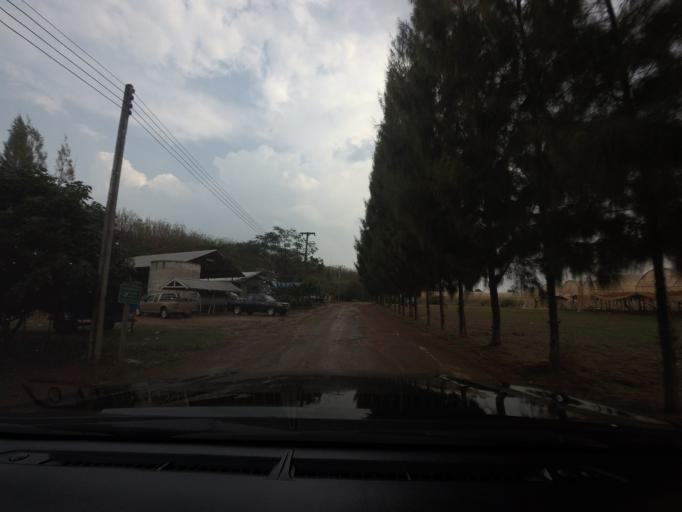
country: TH
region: Nakhon Ratchasima
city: Wang Nam Khiao
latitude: 14.4142
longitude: 101.7382
